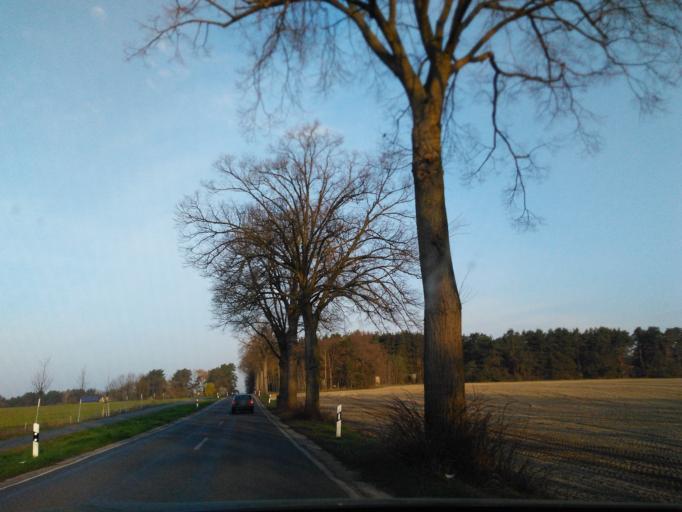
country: DE
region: Brandenburg
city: Strausberg
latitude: 52.5698
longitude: 13.9106
